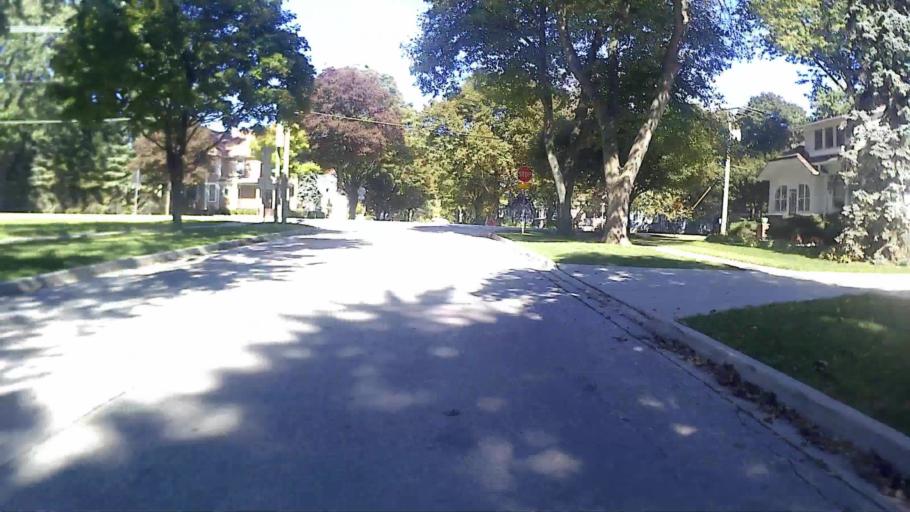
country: US
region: Illinois
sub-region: DuPage County
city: Itasca
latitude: 41.9676
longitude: -88.0146
